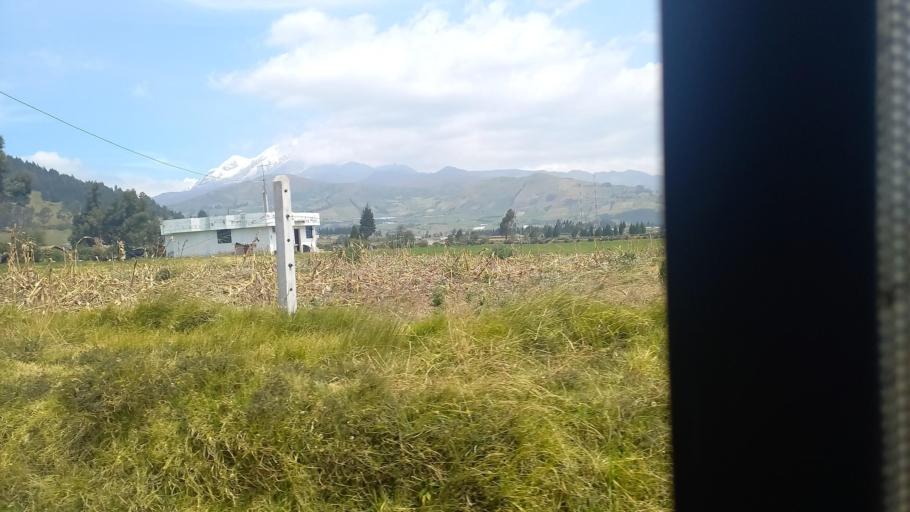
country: EC
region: Pichincha
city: Cayambe
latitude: 0.1576
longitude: -78.0713
